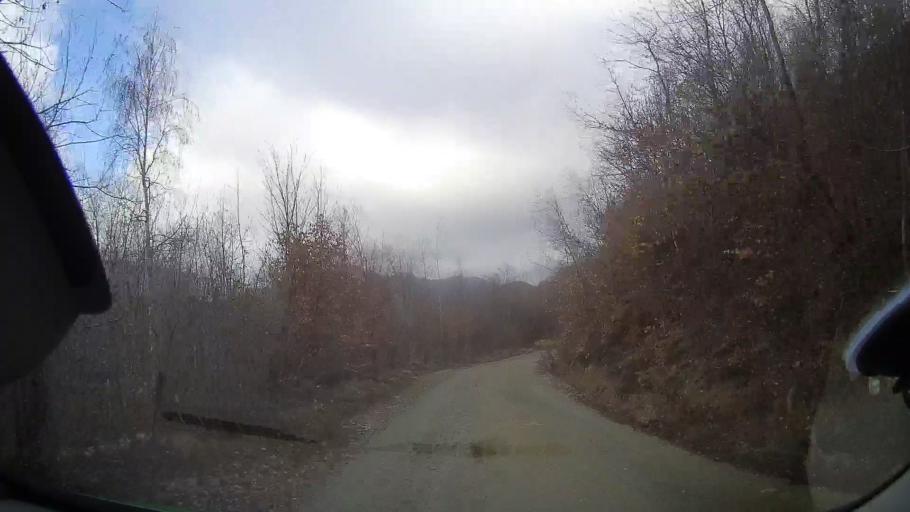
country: RO
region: Cluj
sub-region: Comuna Valea Ierii
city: Valea Ierii
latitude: 46.6774
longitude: 23.3141
